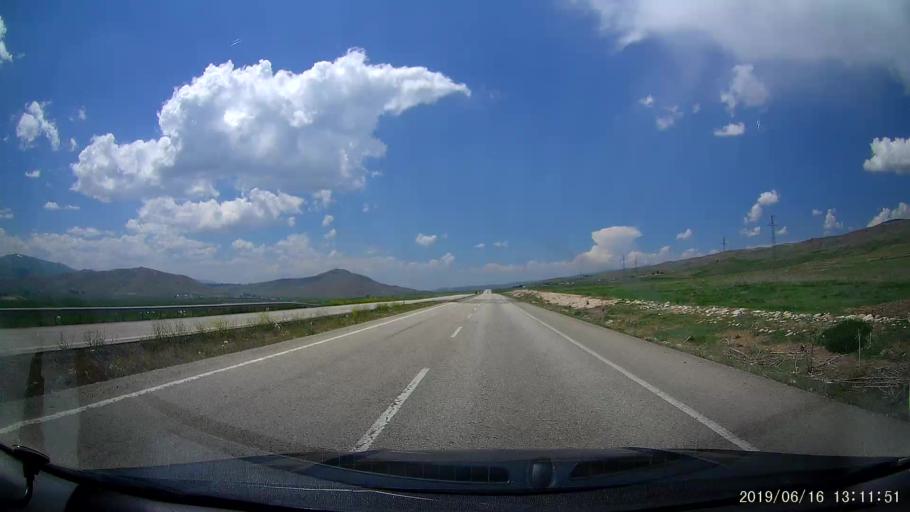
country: TR
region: Agri
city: Diyadin
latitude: 39.5945
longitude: 43.5957
